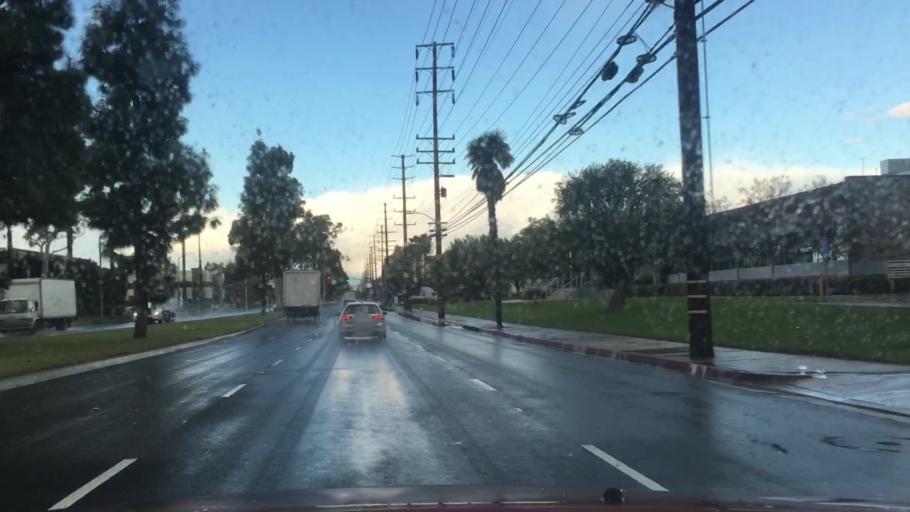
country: US
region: California
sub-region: Orange County
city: La Palma
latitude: 33.8645
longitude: -118.0286
